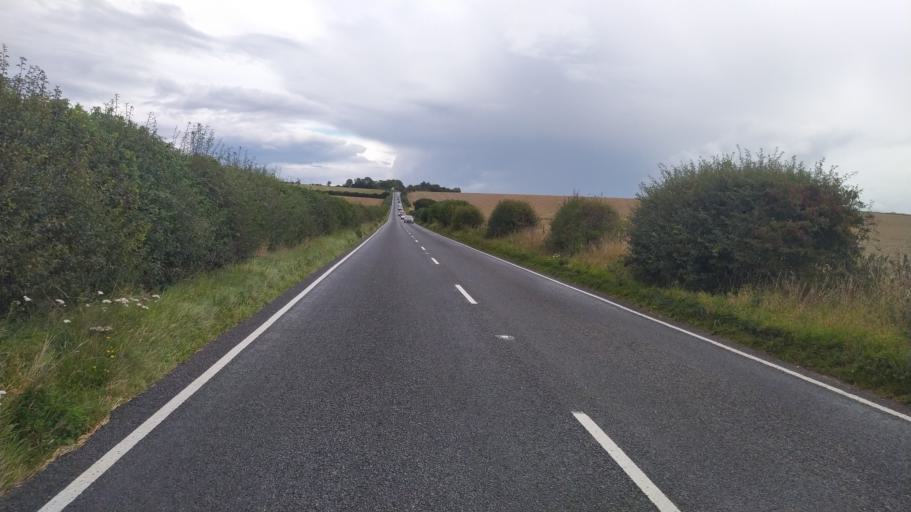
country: GB
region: England
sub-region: Wiltshire
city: Bower Chalke
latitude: 50.9433
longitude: -1.9936
